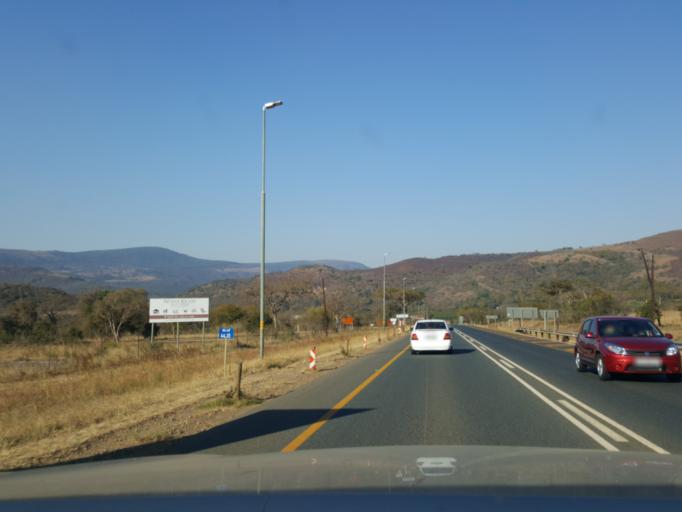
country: ZA
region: Mpumalanga
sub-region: Ehlanzeni District
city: Lydenburg
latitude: -25.3935
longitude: 30.5649
